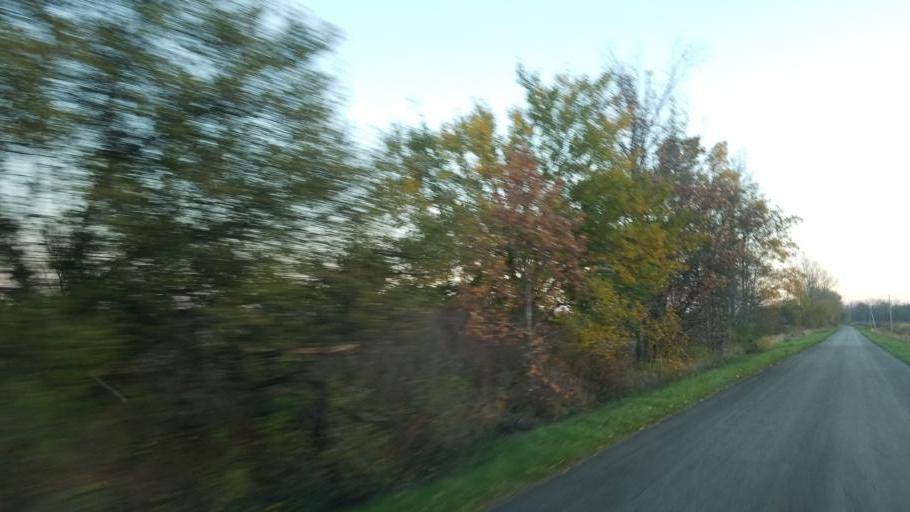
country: US
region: Ohio
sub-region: Huron County
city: Willard
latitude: 41.0310
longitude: -82.7819
